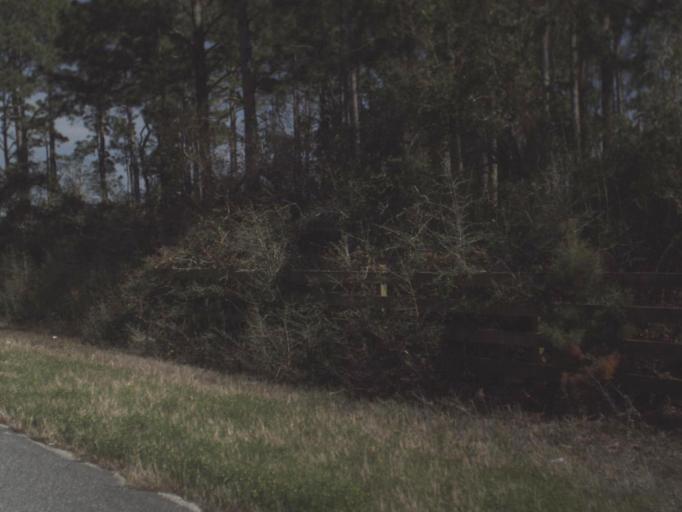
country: US
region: Florida
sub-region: Franklin County
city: Carrabelle
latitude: 29.7906
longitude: -84.7623
